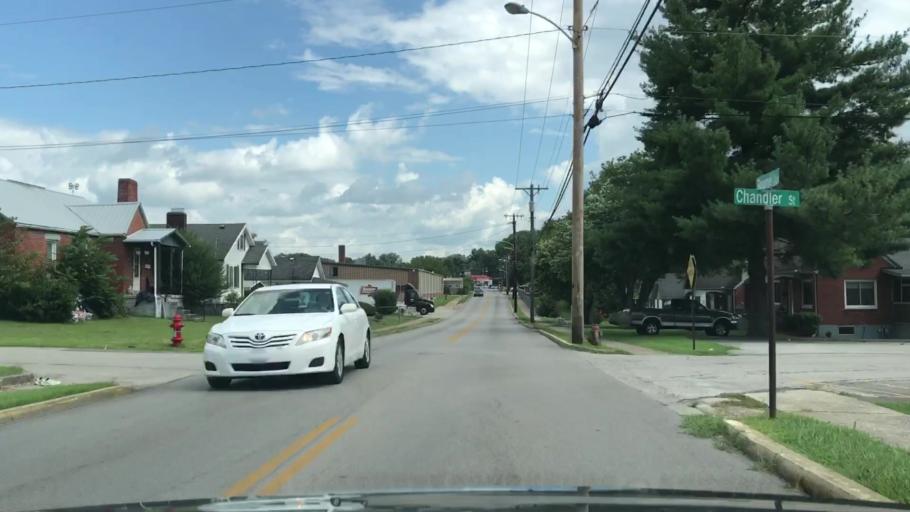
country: US
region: Kentucky
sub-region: Pulaski County
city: Somerset
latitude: 37.0831
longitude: -84.6023
